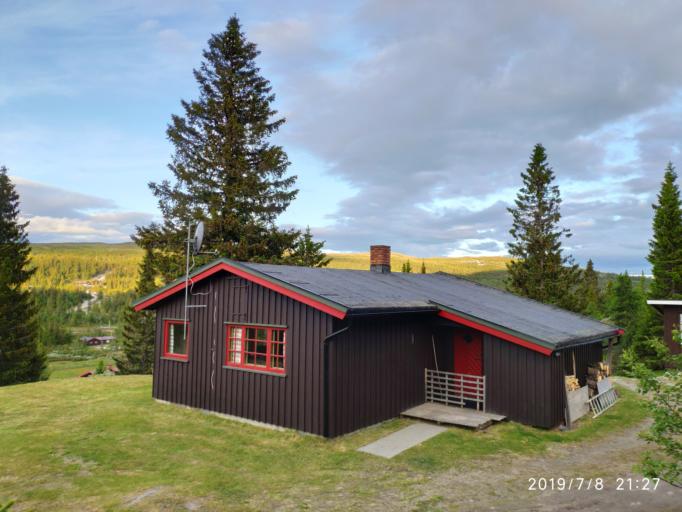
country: NO
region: Buskerud
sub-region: Nes
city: Nesbyen
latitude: 60.3632
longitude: 9.1852
